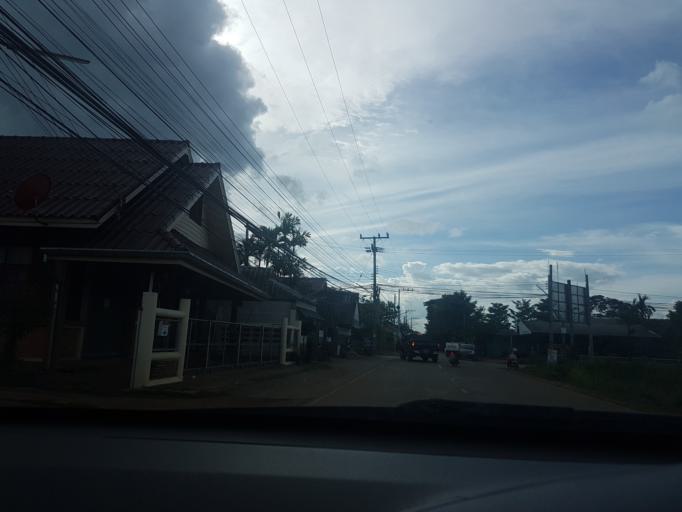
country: TH
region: Lampang
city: Ko Kha
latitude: 18.2116
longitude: 99.4159
